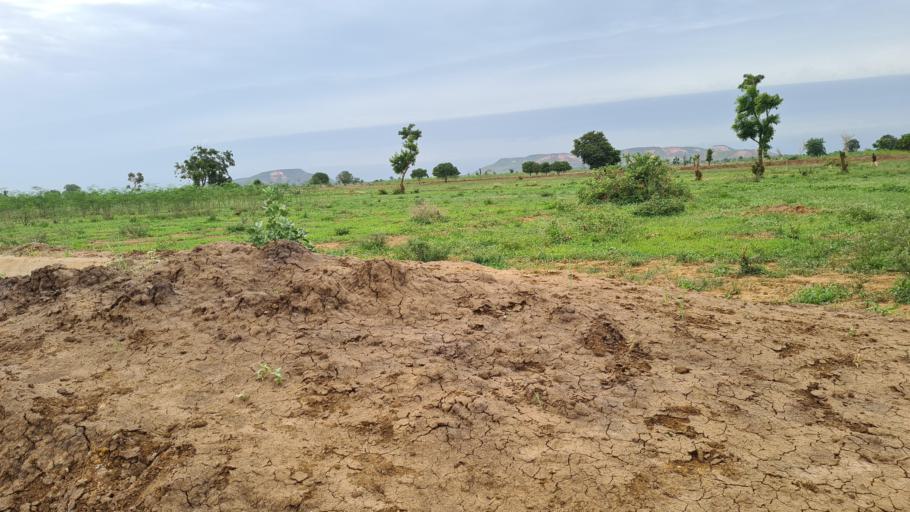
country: NE
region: Tahoua
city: Birni N Konni
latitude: 13.8293
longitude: 5.2639
